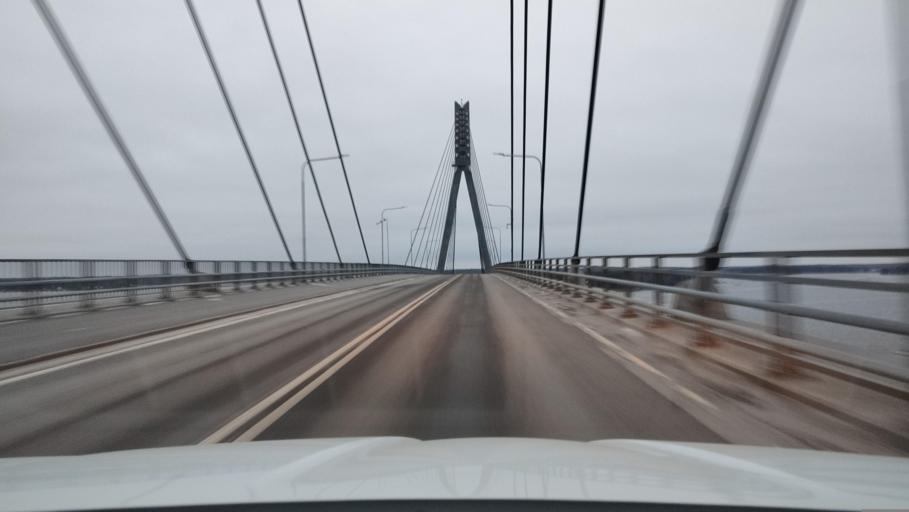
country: FI
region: Ostrobothnia
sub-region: Vaasa
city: Replot
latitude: 63.2069
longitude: 21.4719
